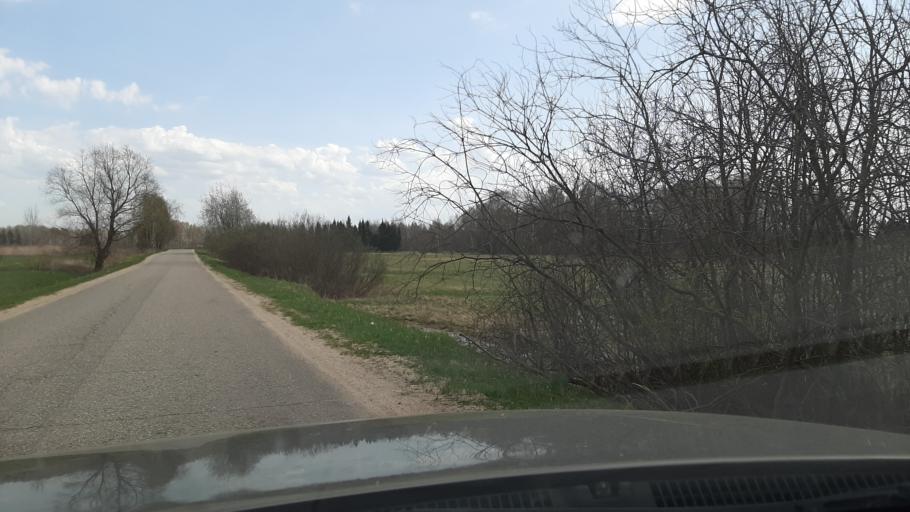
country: RU
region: Ivanovo
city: Furmanov
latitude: 57.2963
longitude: 41.1731
